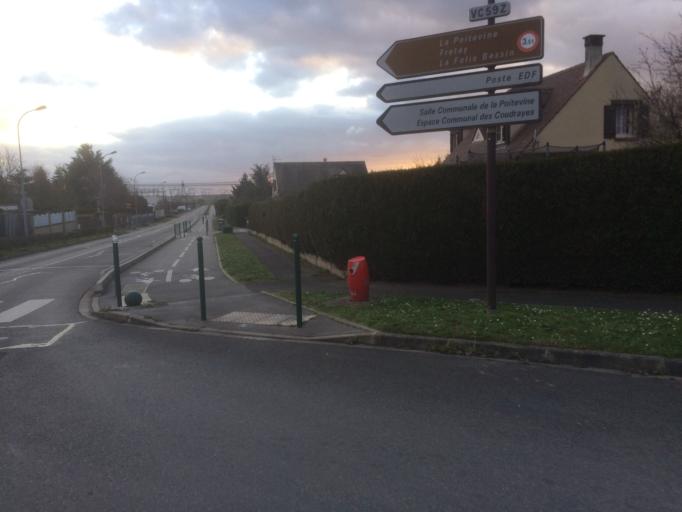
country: FR
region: Ile-de-France
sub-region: Departement de l'Essonne
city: Villejust
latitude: 48.6806
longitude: 2.2325
